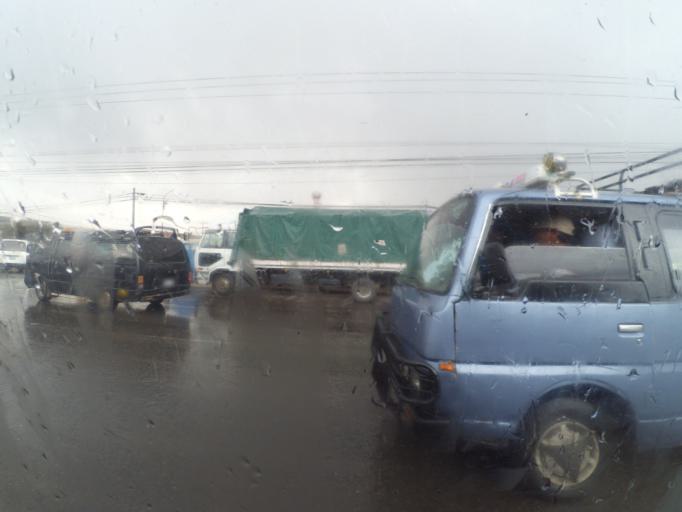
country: BO
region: La Paz
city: La Paz
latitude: -16.5265
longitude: -68.1704
